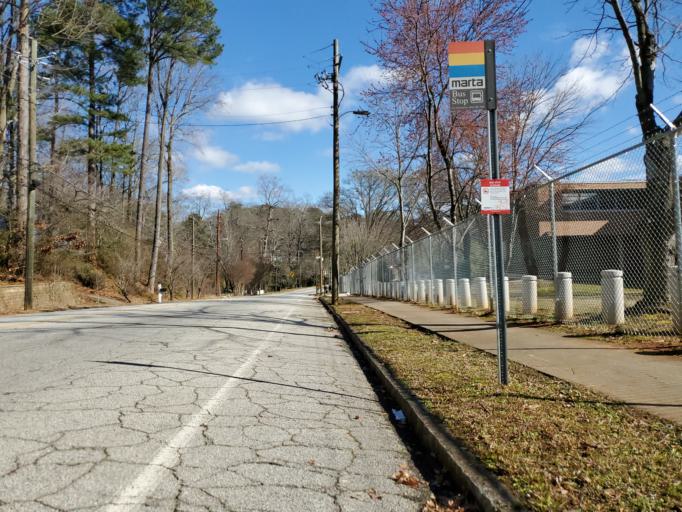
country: US
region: Georgia
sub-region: Fulton County
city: Atlanta
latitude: 33.7264
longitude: -84.3557
